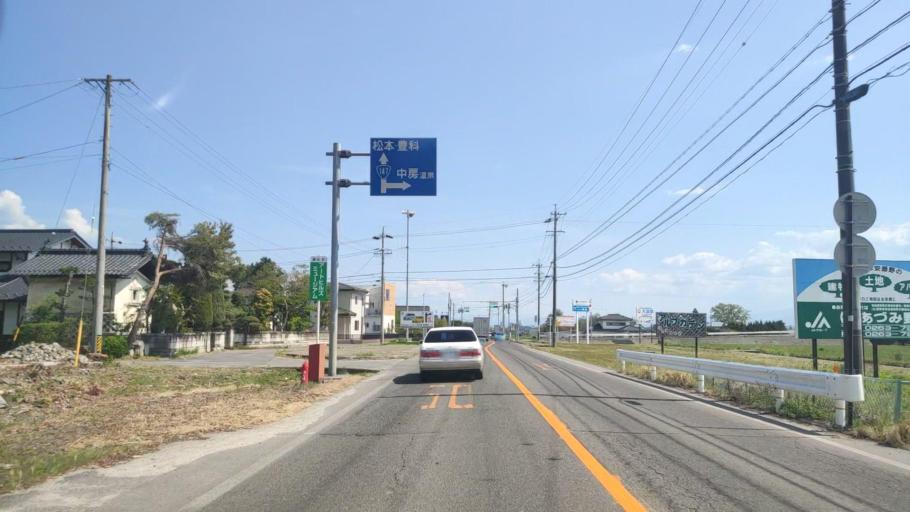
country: JP
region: Nagano
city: Hotaka
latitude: 36.3811
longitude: 137.8678
